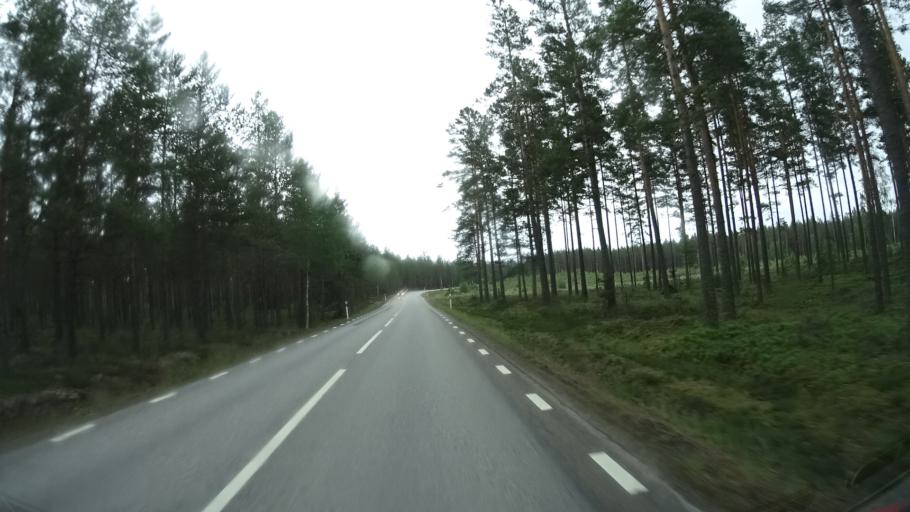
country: SE
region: Kalmar
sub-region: Hultsfreds Kommun
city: Hultsfred
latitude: 57.5273
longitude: 15.7914
